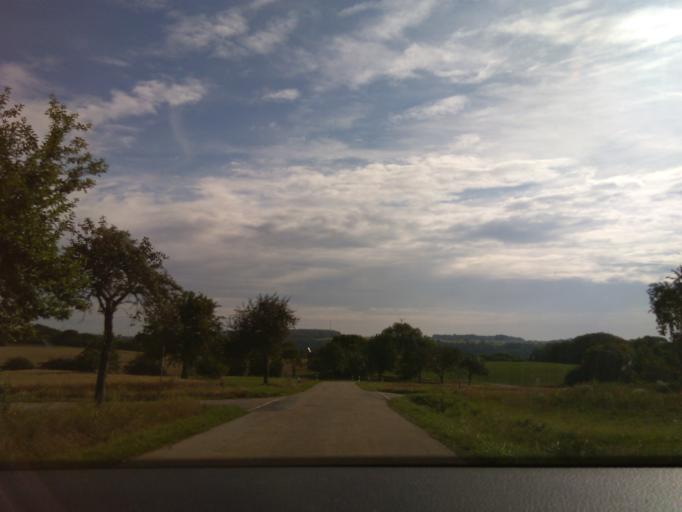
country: DE
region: Baden-Wuerttemberg
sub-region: Regierungsbezirk Stuttgart
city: Langenburg
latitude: 49.2289
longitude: 9.8426
